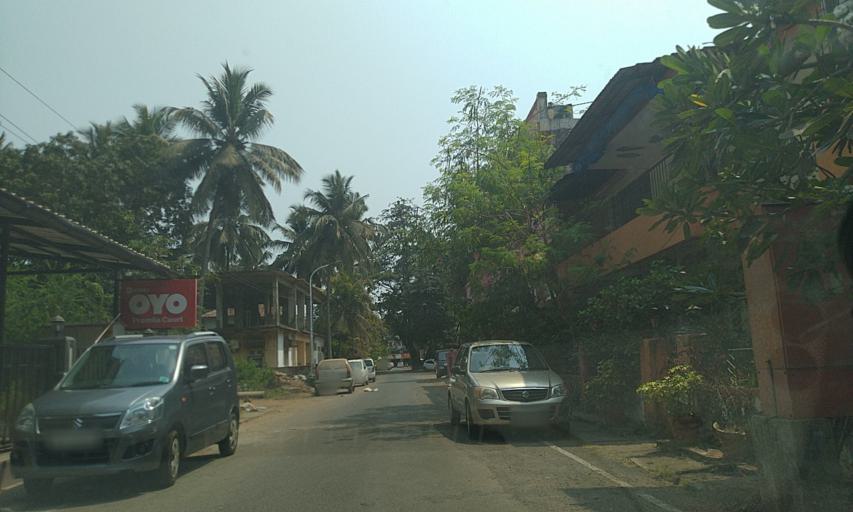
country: IN
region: Goa
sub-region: North Goa
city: Panaji
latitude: 15.4844
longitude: 73.8131
